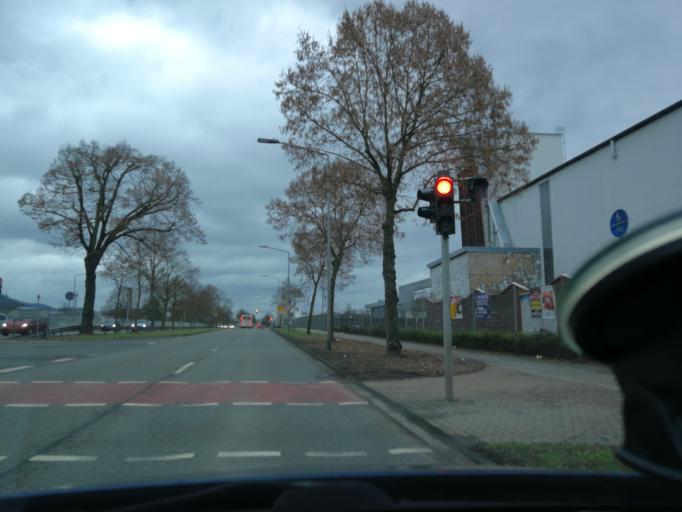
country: DE
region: Rheinland-Pfalz
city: Konz
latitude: 49.7306
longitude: 6.6057
